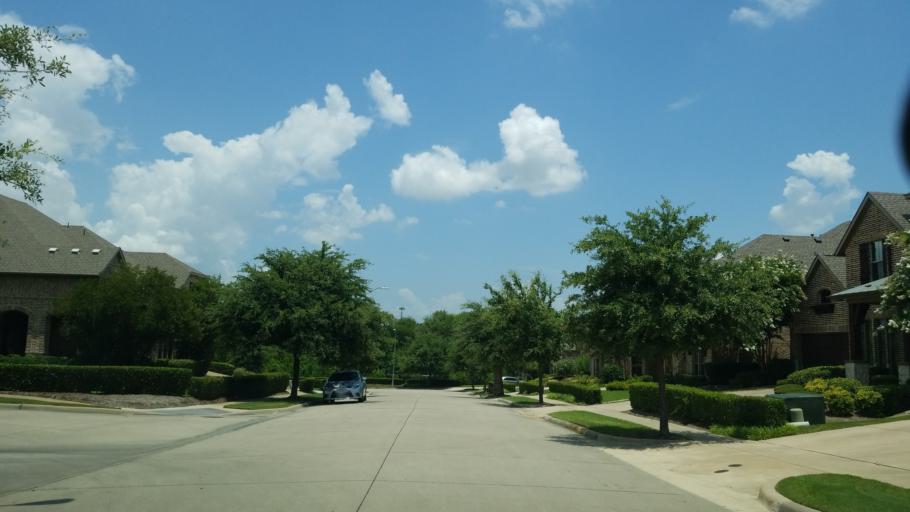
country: US
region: Texas
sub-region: Dallas County
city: Coppell
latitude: 32.9487
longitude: -96.9600
